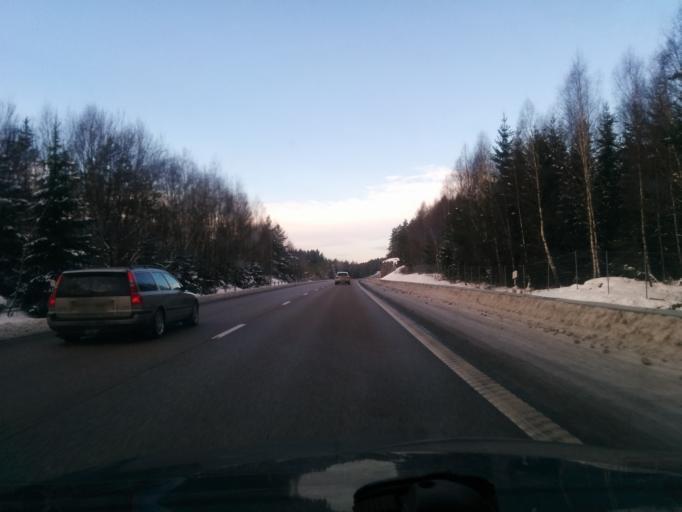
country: SE
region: Stockholm
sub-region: Upplands-Bro Kommun
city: Bro
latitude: 59.5464
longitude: 17.6007
